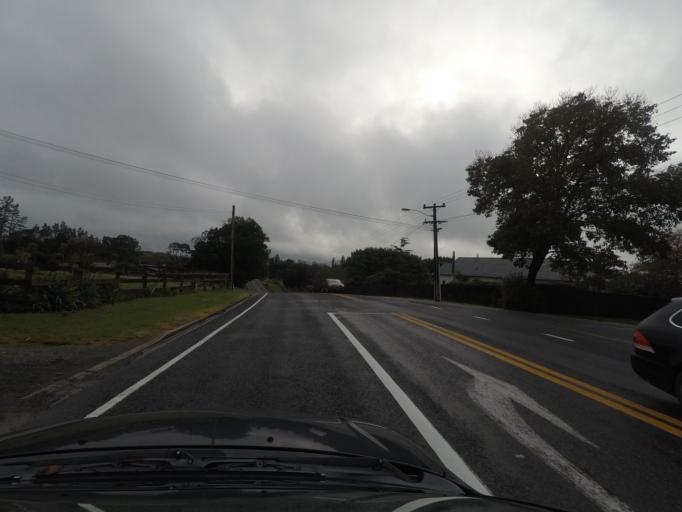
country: NZ
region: Auckland
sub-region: Auckland
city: Rosebank
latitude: -36.7798
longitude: 174.5862
